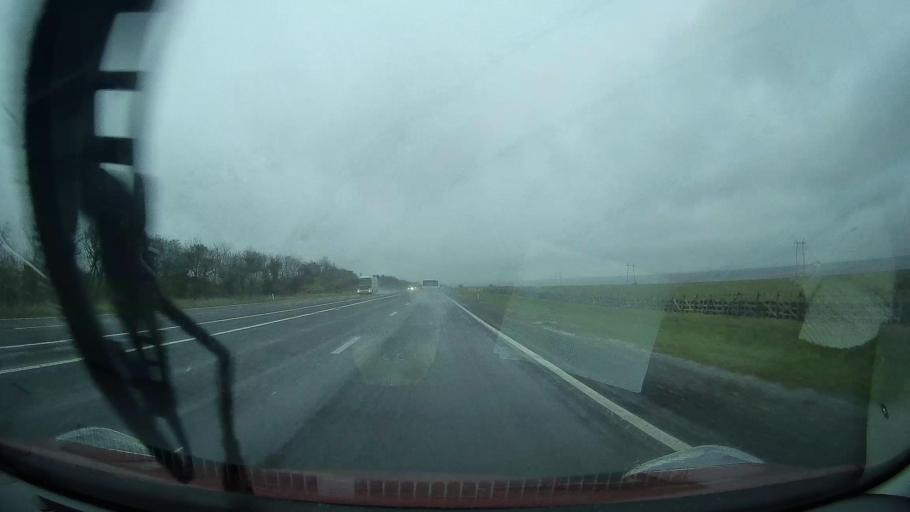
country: RU
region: Stavropol'skiy
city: Nevinnomyssk
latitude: 44.6116
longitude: 42.1198
